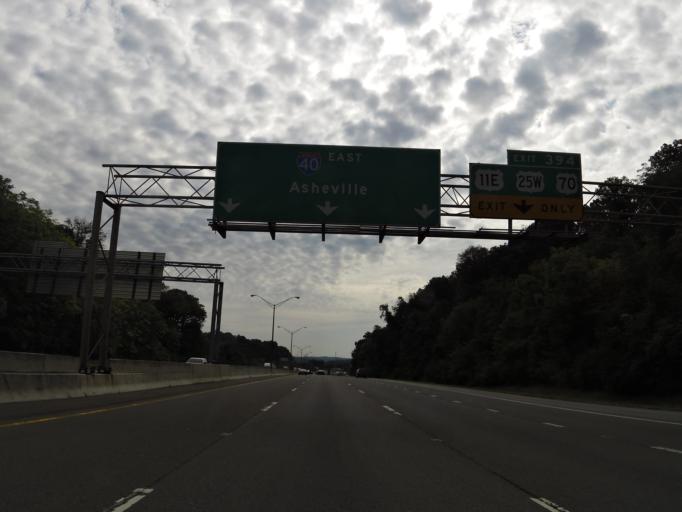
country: US
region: Tennessee
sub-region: Knox County
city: Knoxville
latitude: 36.0122
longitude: -83.8493
